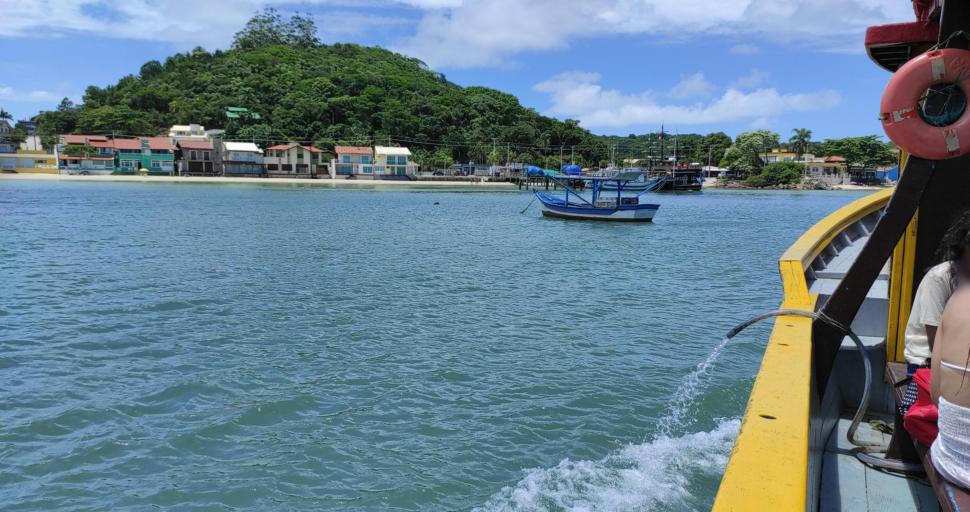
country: BR
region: Santa Catarina
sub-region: Porto Belo
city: Porto Belo
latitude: -27.1826
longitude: -48.5232
